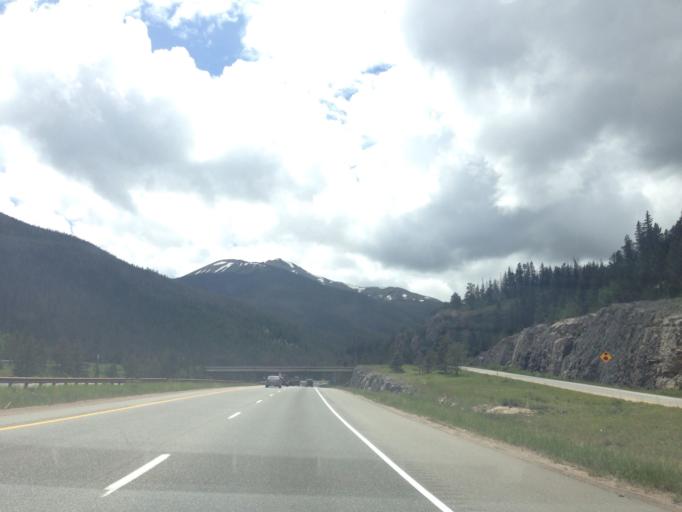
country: US
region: Colorado
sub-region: Clear Creek County
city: Georgetown
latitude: 39.6933
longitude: -105.8025
